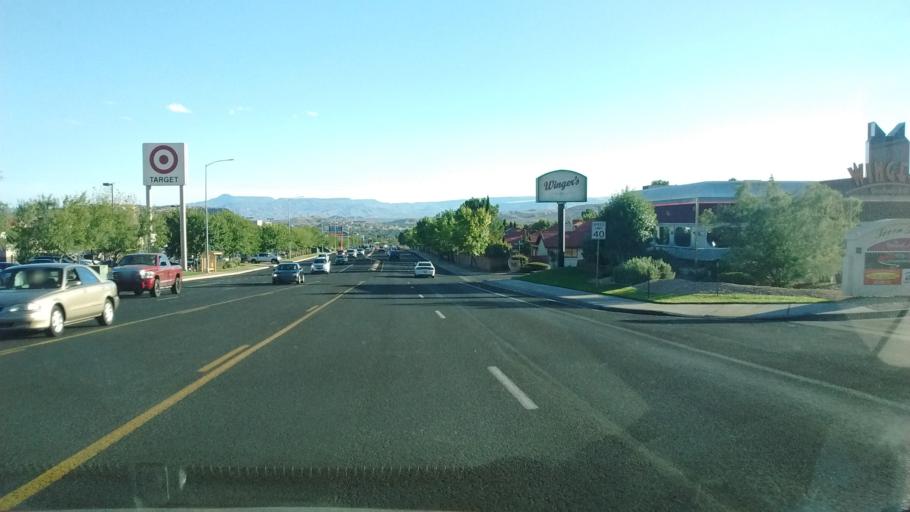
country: US
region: Utah
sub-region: Washington County
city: Saint George
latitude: 37.1053
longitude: -113.5557
